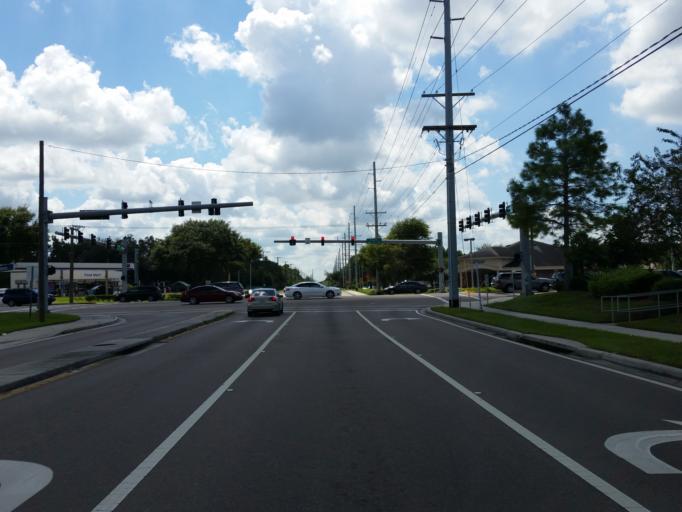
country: US
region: Florida
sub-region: Hillsborough County
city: Riverview
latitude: 27.8543
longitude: -82.3022
